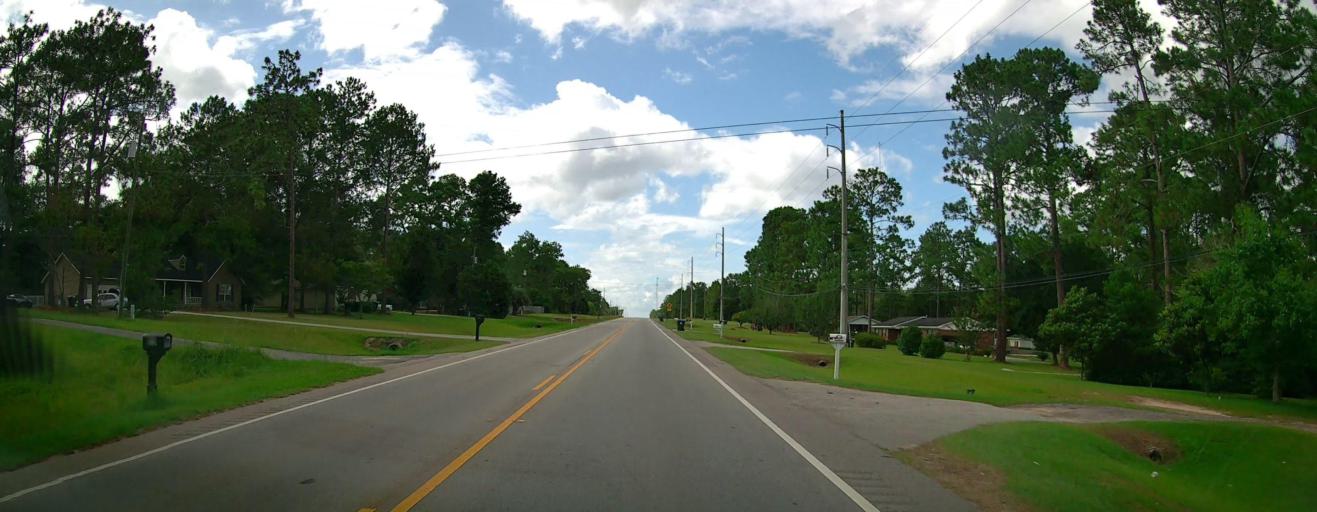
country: US
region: Georgia
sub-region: Coffee County
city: Douglas
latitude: 31.5198
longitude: -82.8717
